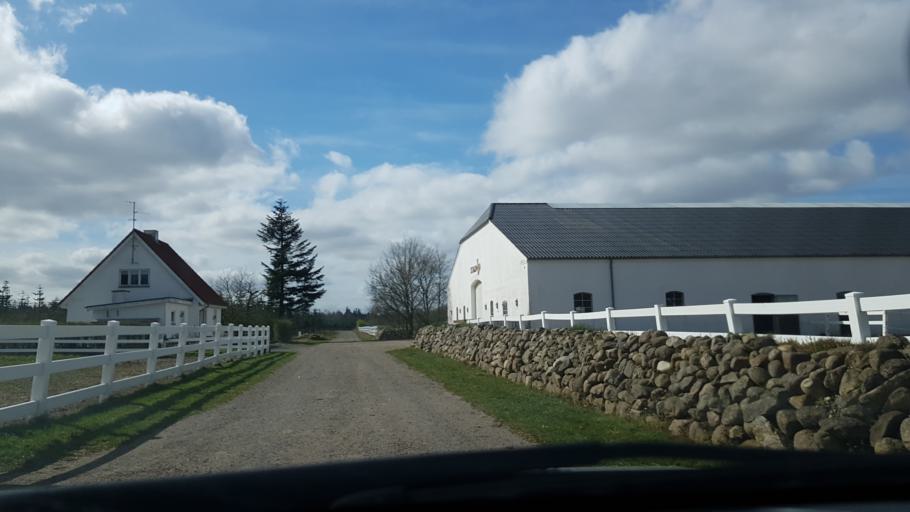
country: DK
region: South Denmark
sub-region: Haderslev Kommune
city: Gram
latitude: 55.2987
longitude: 8.9833
